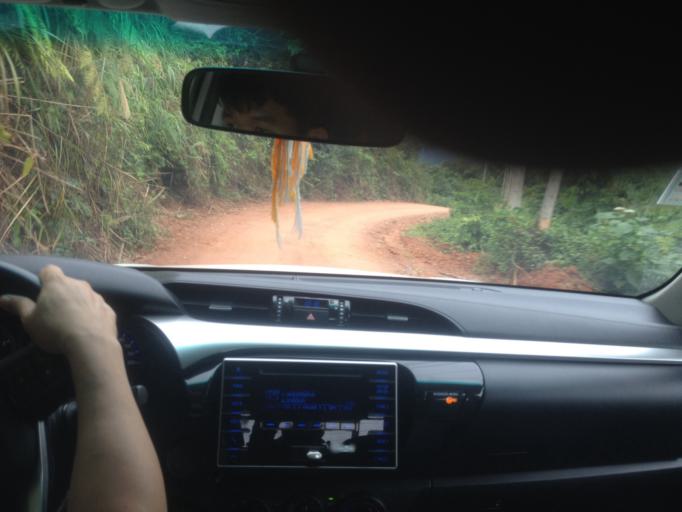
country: TH
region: Nan
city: Chaloem Phra Kiat
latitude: 19.9670
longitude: 101.1385
